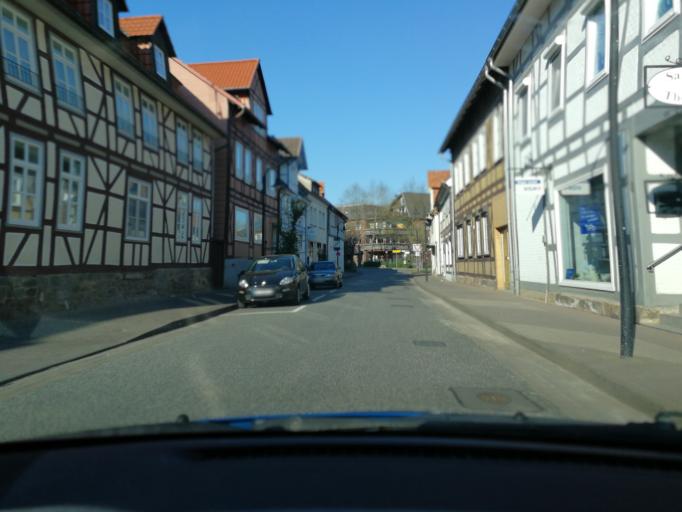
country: DE
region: Lower Saxony
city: Adelebsen
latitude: 51.5798
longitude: 9.7558
